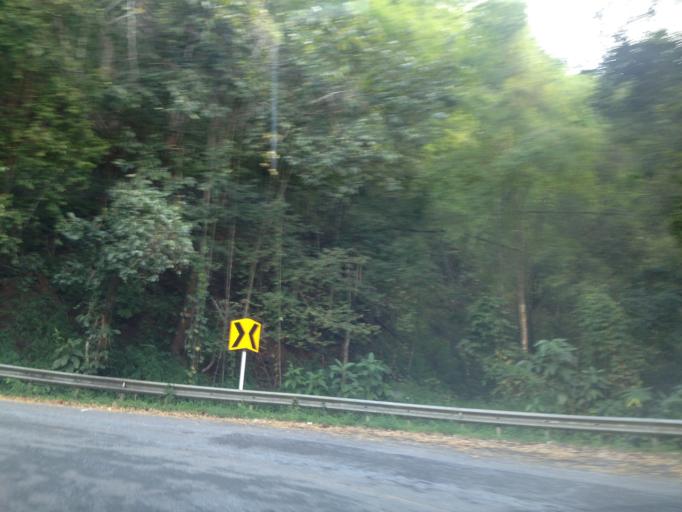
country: TH
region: Chiang Mai
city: Samoeng
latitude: 18.8042
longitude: 98.8025
